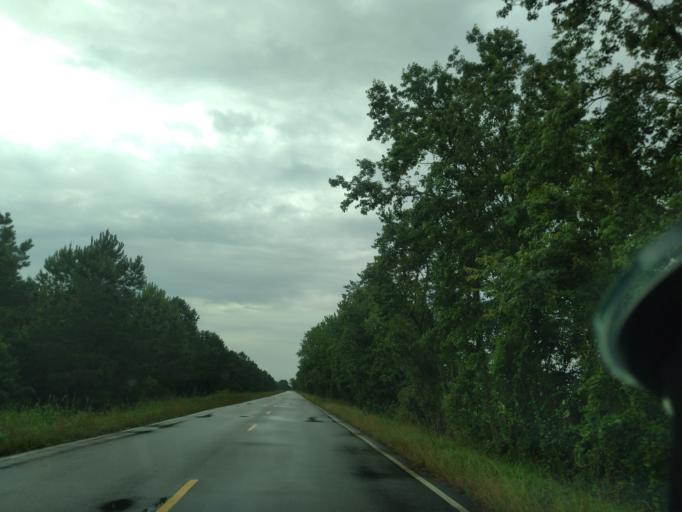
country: US
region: North Carolina
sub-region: Washington County
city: Plymouth
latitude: 35.8472
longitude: -76.5583
